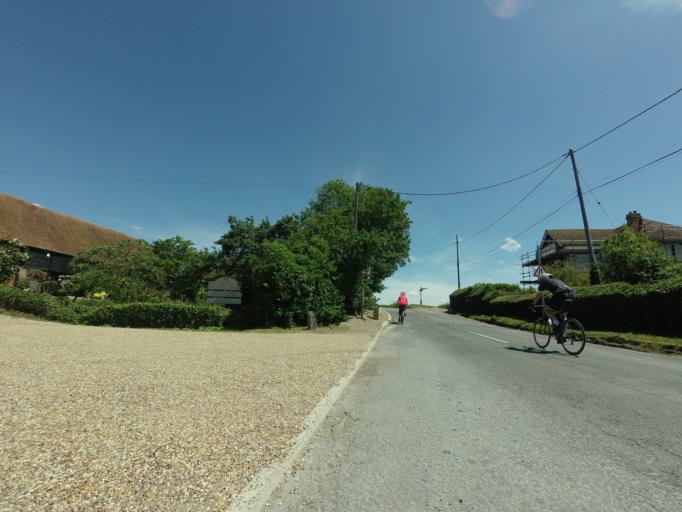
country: GB
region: England
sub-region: Medway
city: Cooling
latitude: 51.4547
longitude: 0.5231
